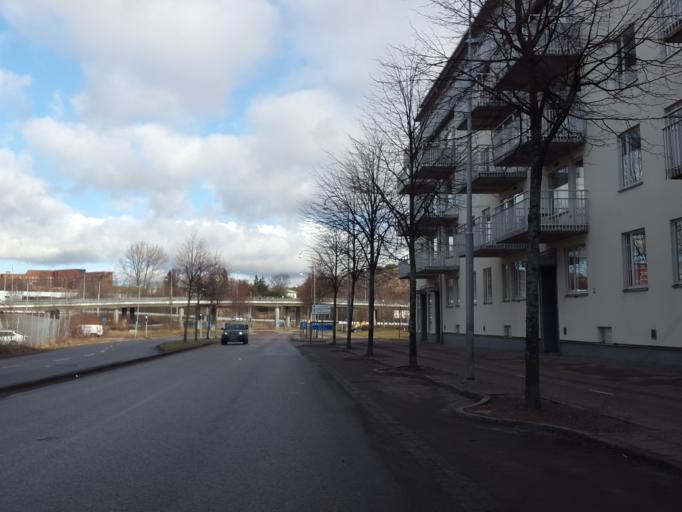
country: SE
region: Vaestra Goetaland
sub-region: Goteborg
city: Majorna
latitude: 57.7080
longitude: 11.9235
